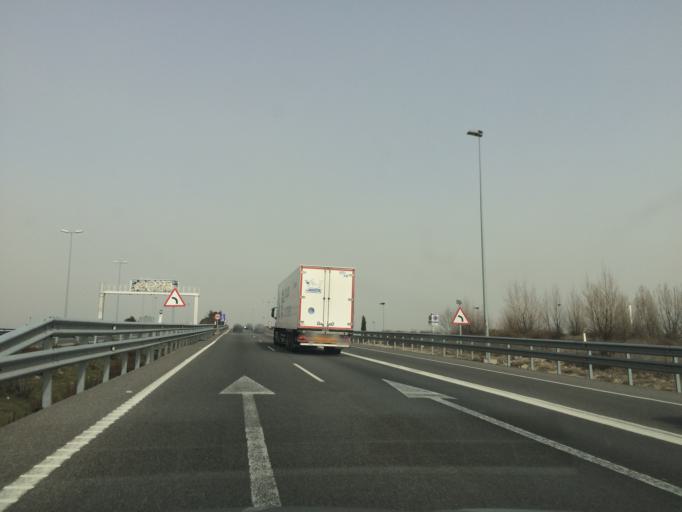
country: ES
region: Madrid
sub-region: Provincia de Madrid
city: Las Rozas de Madrid
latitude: 40.5195
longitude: -3.8892
